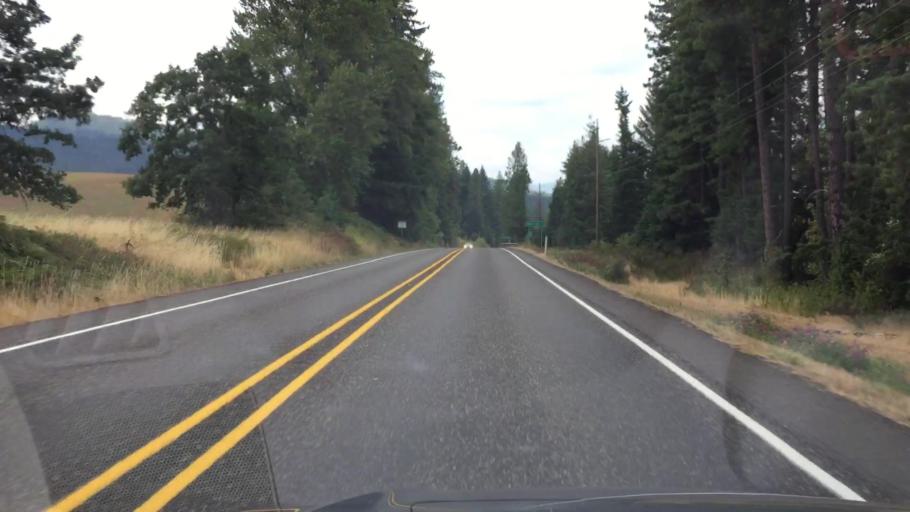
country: US
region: Washington
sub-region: Klickitat County
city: White Salmon
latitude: 45.8021
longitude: -121.4878
